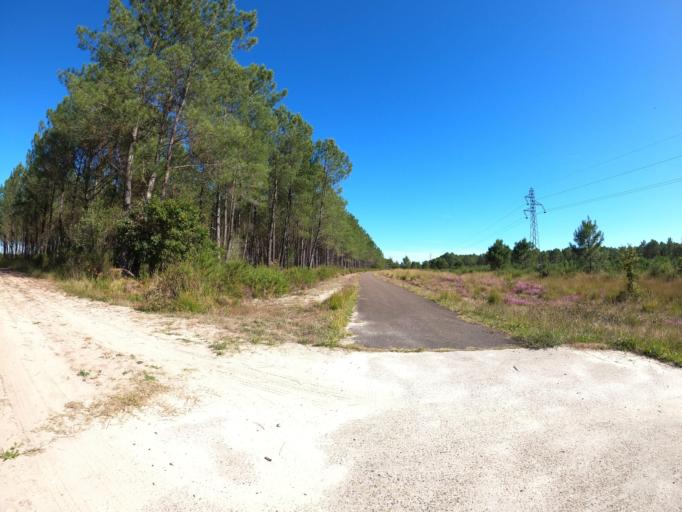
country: FR
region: Aquitaine
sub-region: Departement des Landes
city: Ychoux
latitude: 44.3404
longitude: -0.9676
